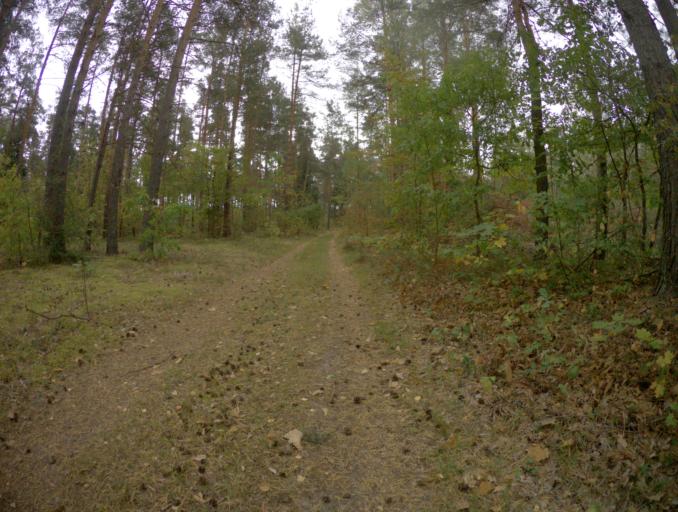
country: RU
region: Vladimir
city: Kosterevo
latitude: 55.8199
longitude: 39.5482
